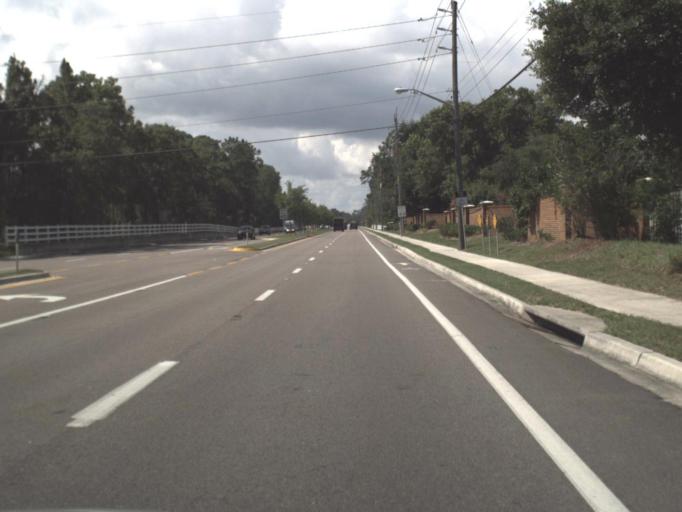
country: US
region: Florida
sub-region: Saint Johns County
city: Fruit Cove
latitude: 30.1014
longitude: -81.6273
